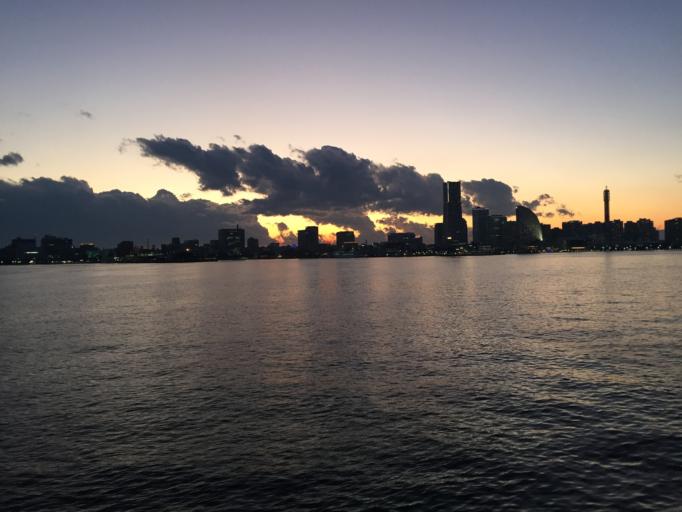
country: JP
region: Kanagawa
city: Yokohama
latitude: 35.4590
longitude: 139.6582
